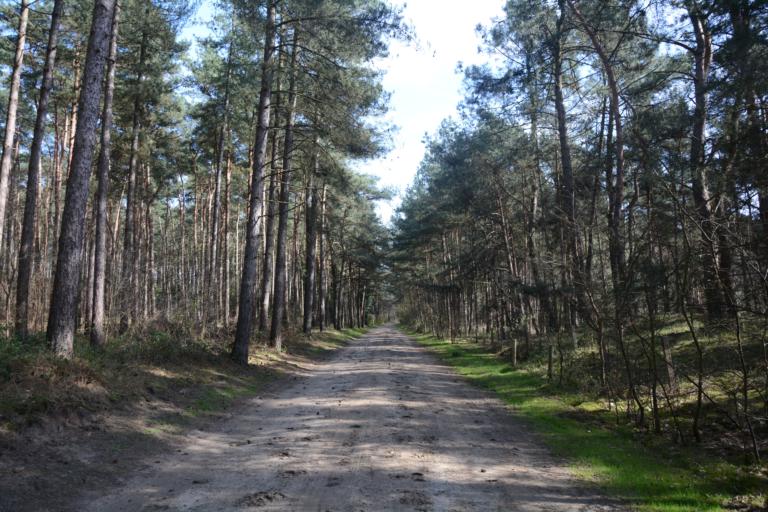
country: BE
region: Flanders
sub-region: Provincie Antwerpen
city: Meerhout
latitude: 51.1442
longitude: 5.0472
